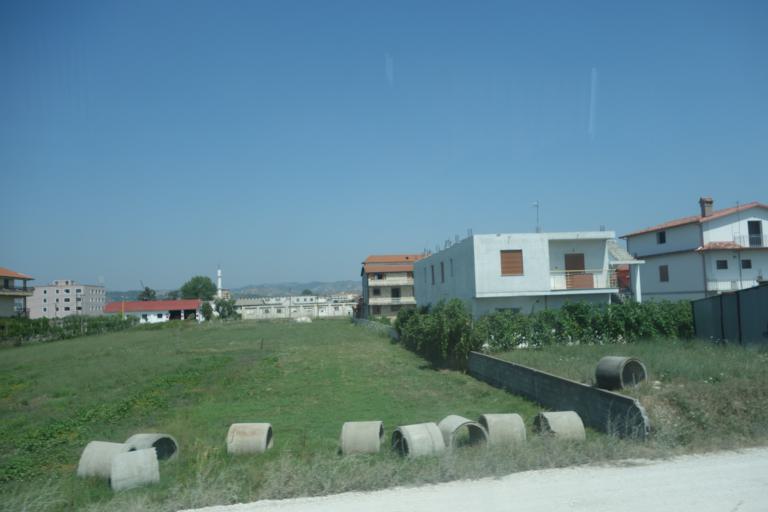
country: AL
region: Tirane
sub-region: Rrethi i Kavajes
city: Synej
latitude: 41.1825
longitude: 19.5448
